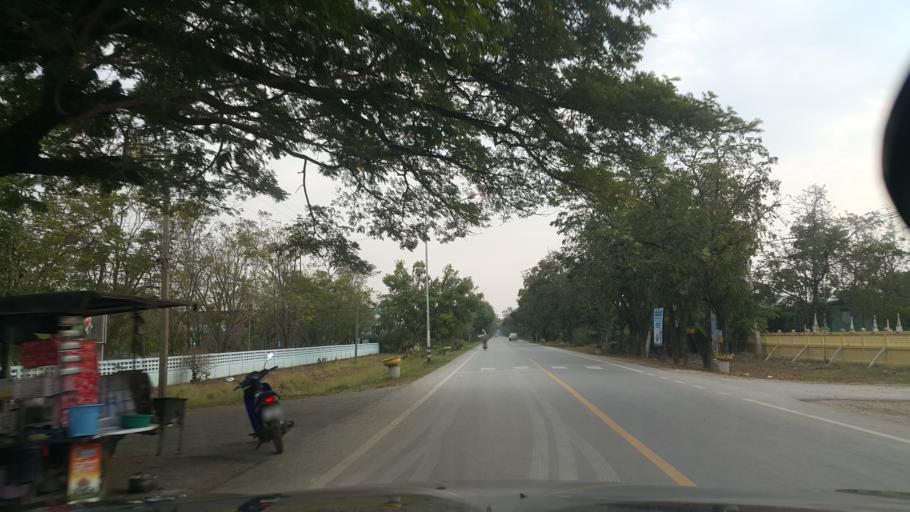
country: TH
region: Sukhothai
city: Si Samrong
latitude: 17.1695
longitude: 99.7141
